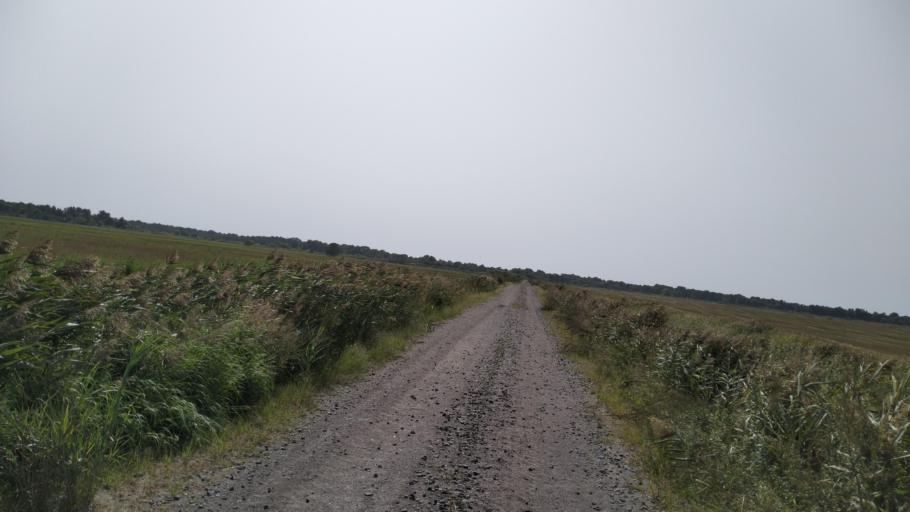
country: BY
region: Brest
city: Davyd-Haradok
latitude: 51.9761
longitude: 27.1745
